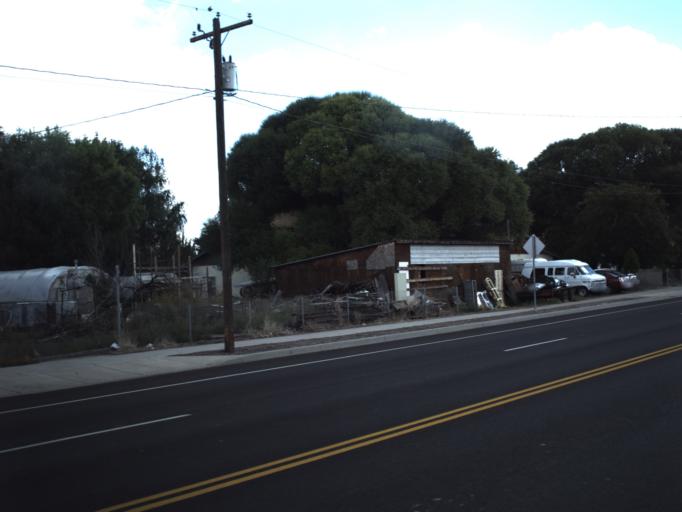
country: US
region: Utah
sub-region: Sevier County
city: Monroe
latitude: 38.6302
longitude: -112.1270
